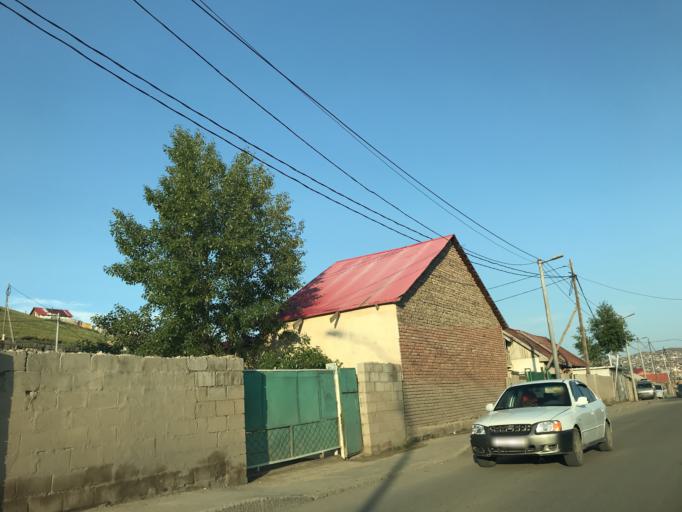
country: MN
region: Ulaanbaatar
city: Ulaanbaatar
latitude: 47.9495
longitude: 106.9351
